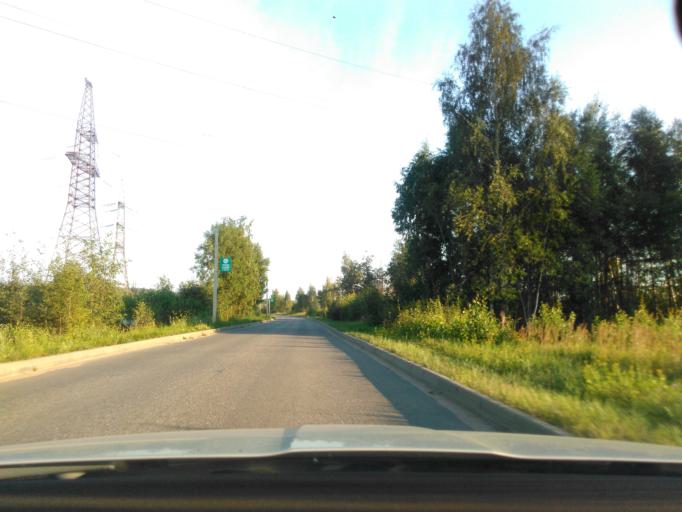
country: RU
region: Tverskaya
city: Konakovo
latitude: 56.7415
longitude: 36.7792
